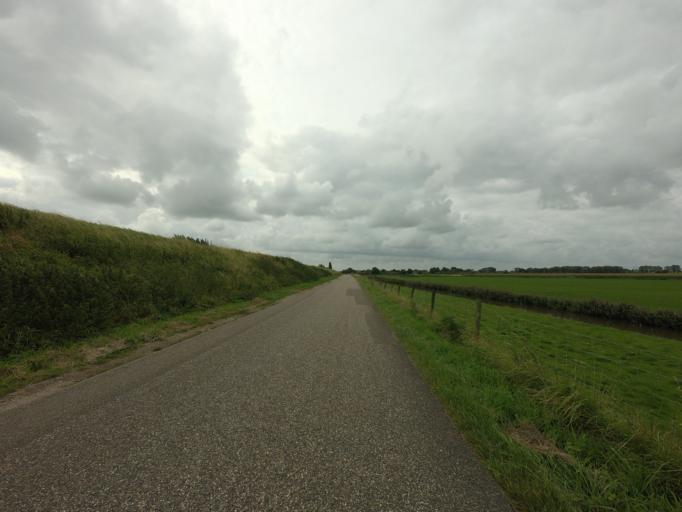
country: NL
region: North Holland
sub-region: Gemeente Hoorn
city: Hoorn
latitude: 52.6070
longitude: 5.0158
